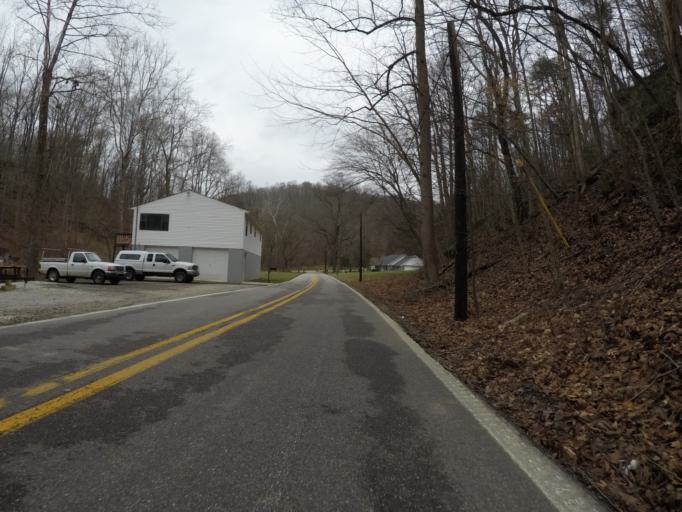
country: US
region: West Virginia
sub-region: Cabell County
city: Barboursville
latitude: 38.4440
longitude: -82.2462
